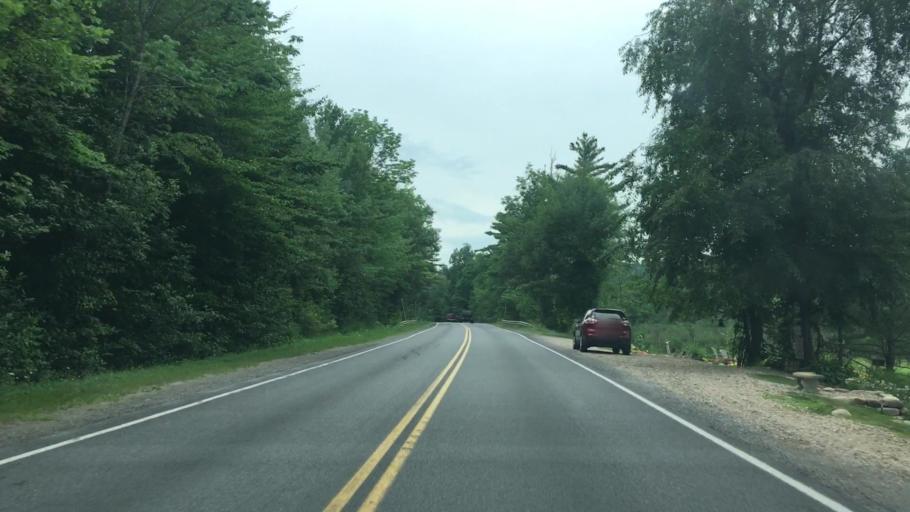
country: US
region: New York
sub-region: Clinton County
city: Peru
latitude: 44.5008
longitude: -73.5898
